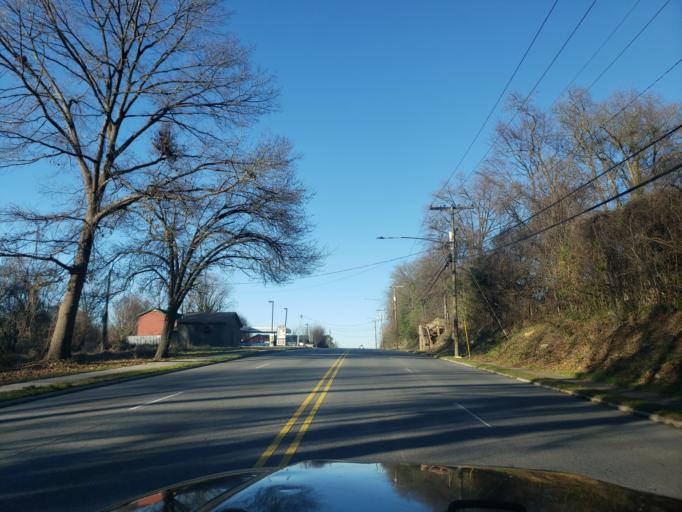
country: US
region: North Carolina
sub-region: Gaston County
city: Gastonia
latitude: 35.2691
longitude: -81.1877
